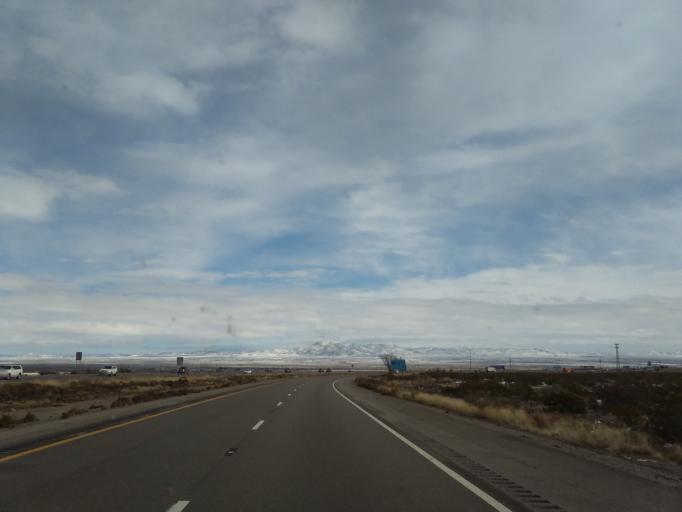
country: US
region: New Mexico
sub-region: Hidalgo County
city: Lordsburg
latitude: 32.3529
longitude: -108.7536
